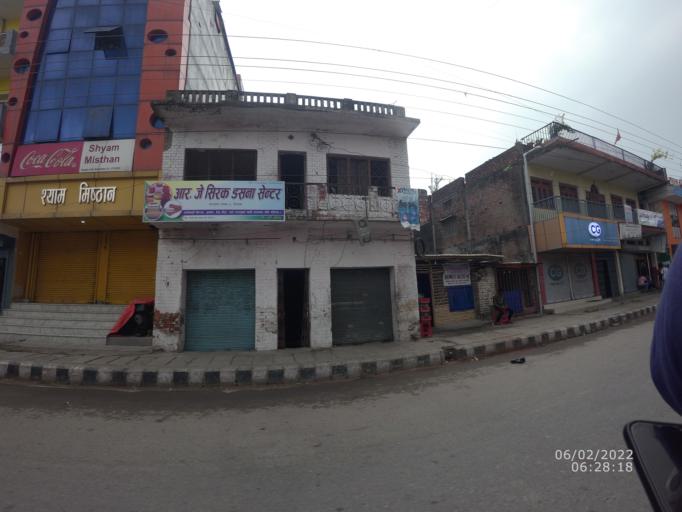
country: NP
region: Western Region
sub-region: Lumbini Zone
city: Bhairahawa
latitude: 27.5147
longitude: 83.4531
